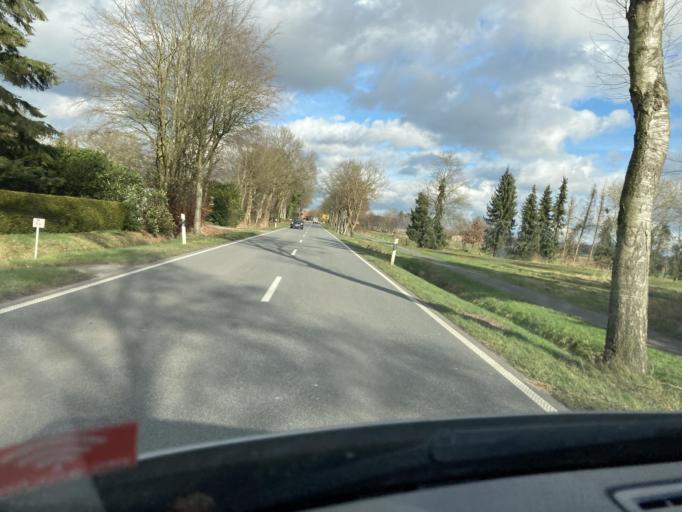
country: DE
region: Lower Saxony
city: Friedeburg
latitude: 53.3931
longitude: 7.8398
